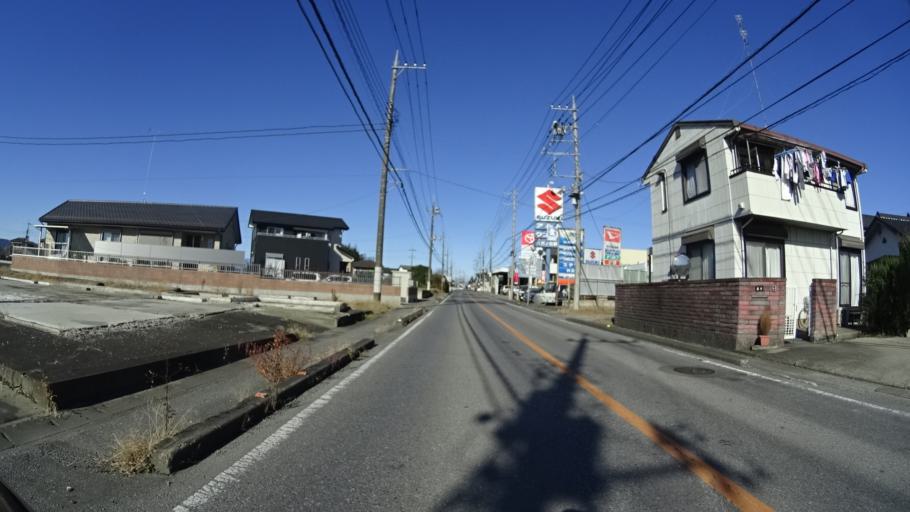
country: JP
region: Tochigi
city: Tochigi
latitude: 36.4176
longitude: 139.7493
